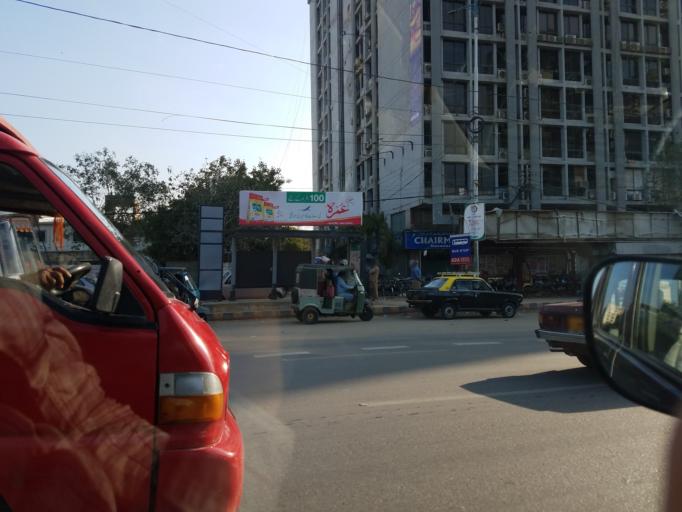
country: PK
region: Sindh
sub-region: Karachi District
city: Karachi
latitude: 24.8625
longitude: 67.0709
